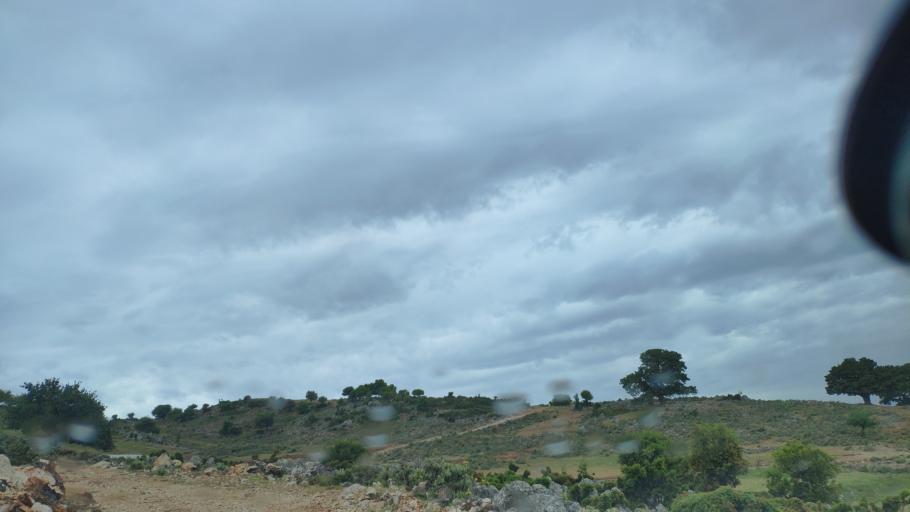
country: GR
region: West Greece
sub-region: Nomos Aitolias kai Akarnanias
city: Archontochorion
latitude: 38.6827
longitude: 21.0225
